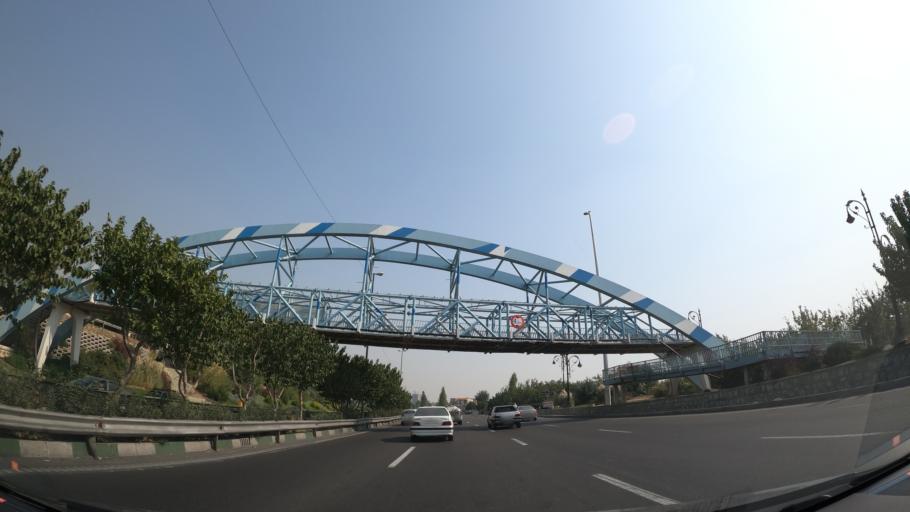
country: IR
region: Tehran
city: Tehran
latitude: 35.7542
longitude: 51.2727
